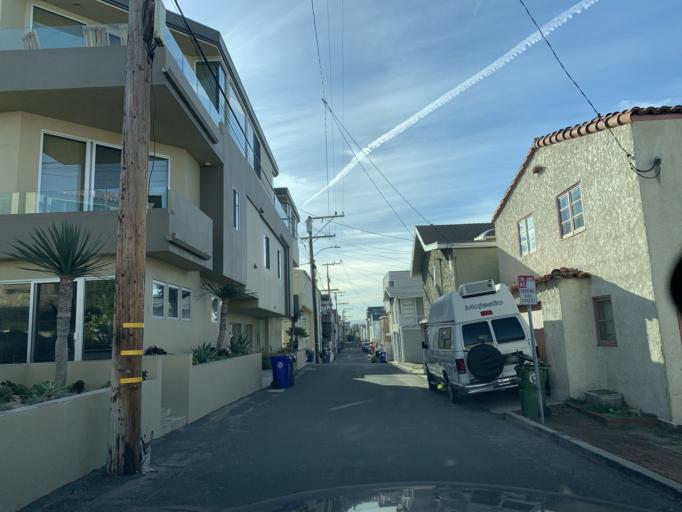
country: US
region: California
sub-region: Los Angeles County
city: Manhattan Beach
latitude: 33.8792
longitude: -118.4074
